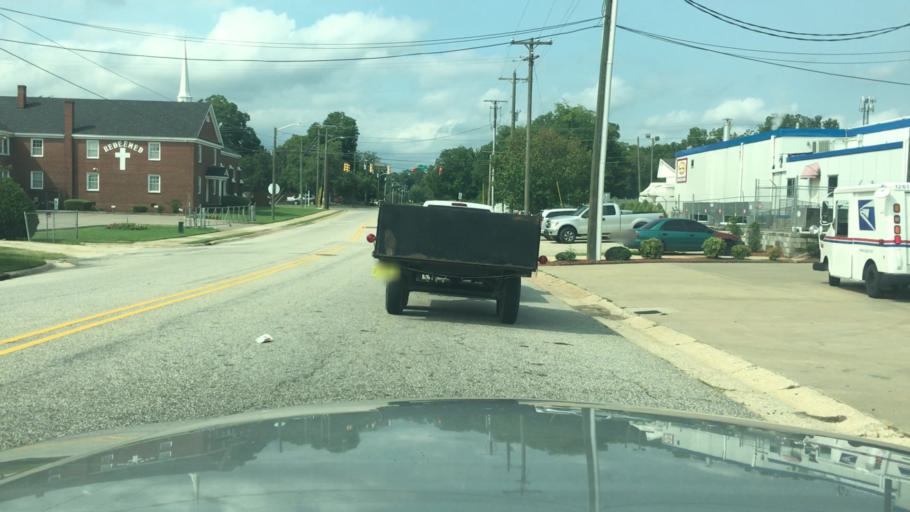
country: US
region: North Carolina
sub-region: Cumberland County
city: Fayetteville
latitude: 35.0464
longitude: -78.8612
